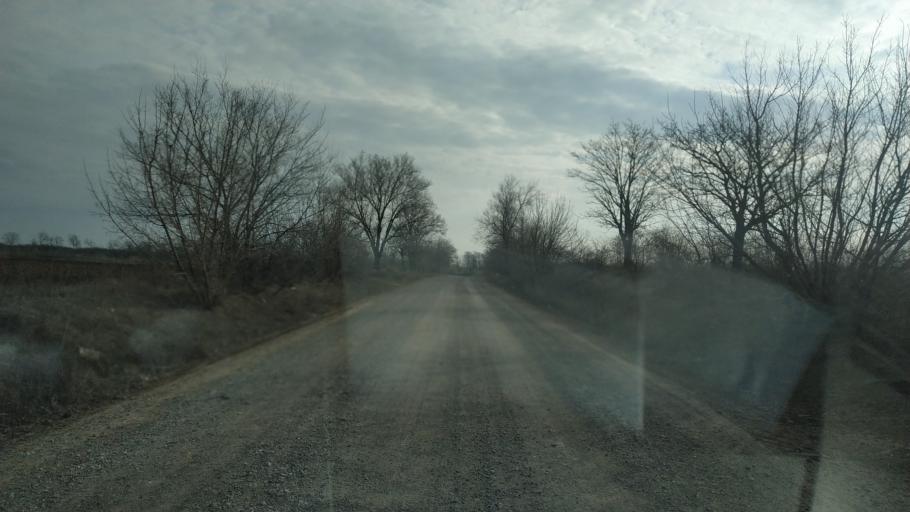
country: MD
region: Chisinau
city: Vadul lui Voda
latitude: 46.9908
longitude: 29.0972
